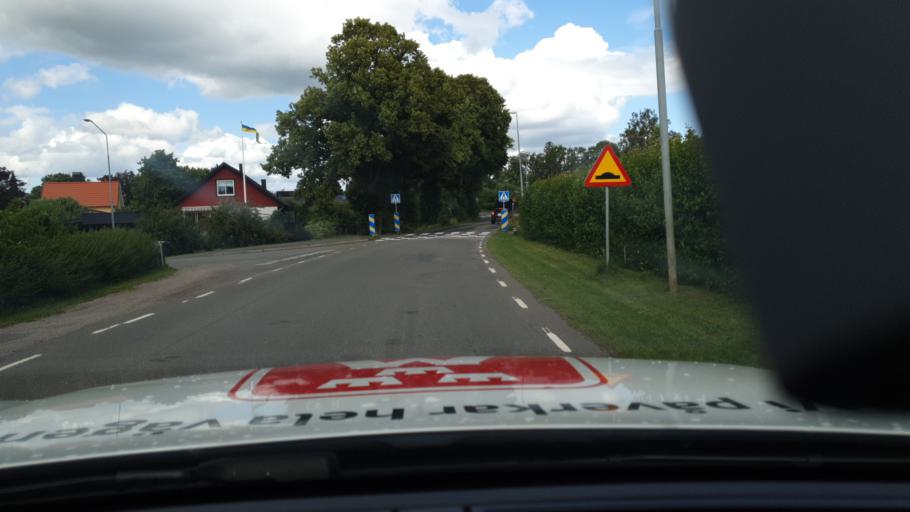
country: SE
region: Vaestra Goetaland
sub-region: Skara Kommun
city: Axvall
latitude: 58.3838
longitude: 13.6472
